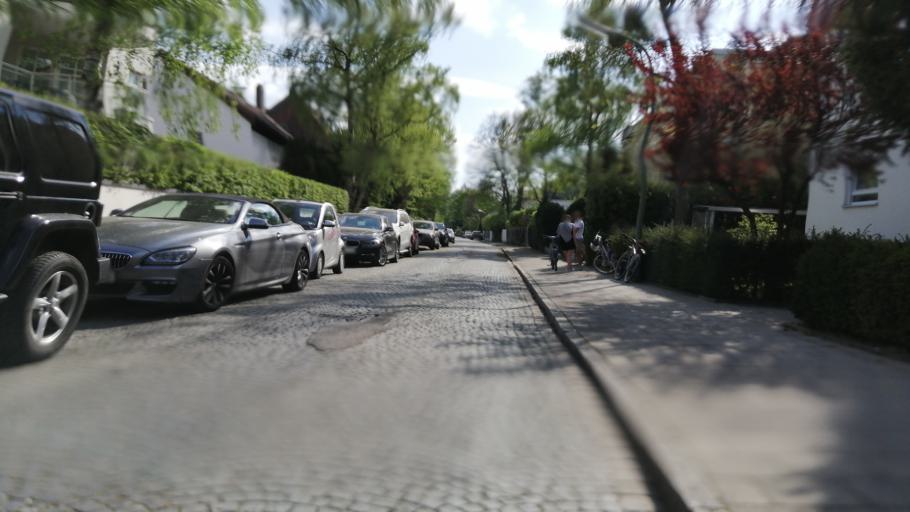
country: DE
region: Bavaria
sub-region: Upper Bavaria
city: Bogenhausen
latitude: 48.1590
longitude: 11.6133
